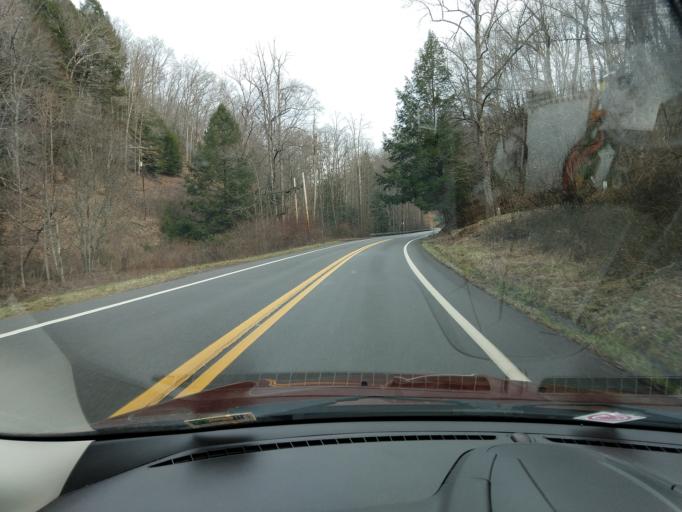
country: US
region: West Virginia
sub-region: Wyoming County
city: Pineville
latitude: 37.5503
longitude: -81.5753
